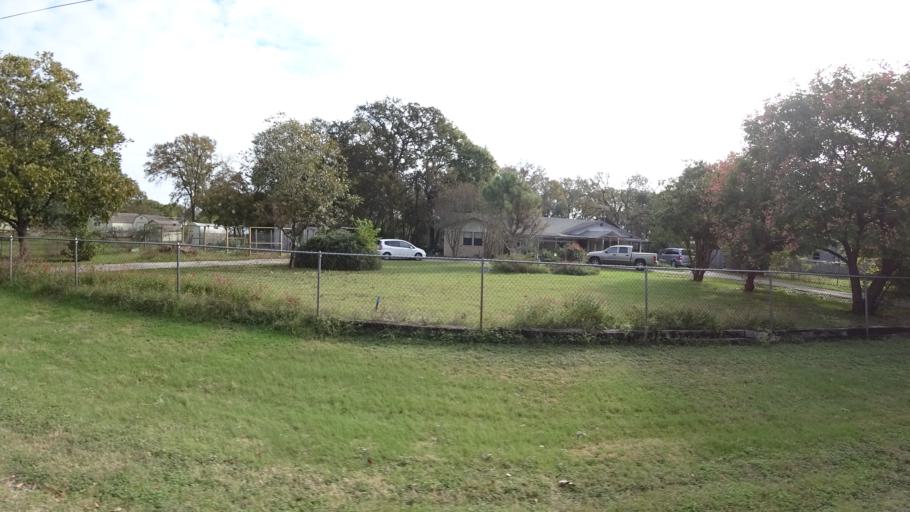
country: US
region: Texas
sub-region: Travis County
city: Manchaca
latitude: 30.1357
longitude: -97.8426
